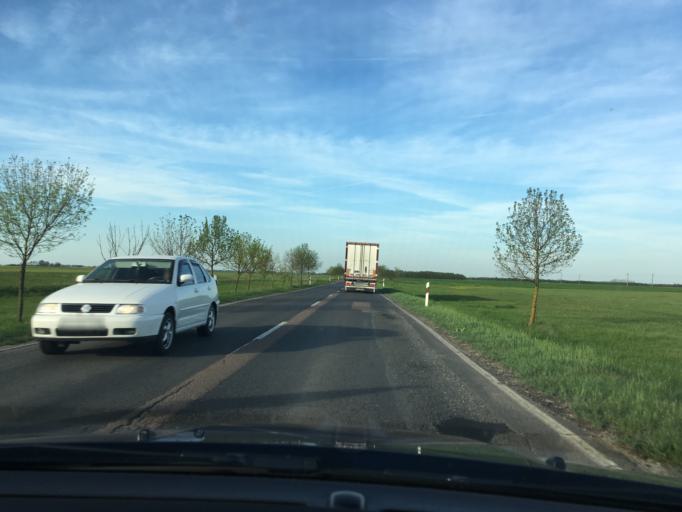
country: HU
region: Hajdu-Bihar
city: Berettyoujfalu
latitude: 47.1544
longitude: 21.4990
